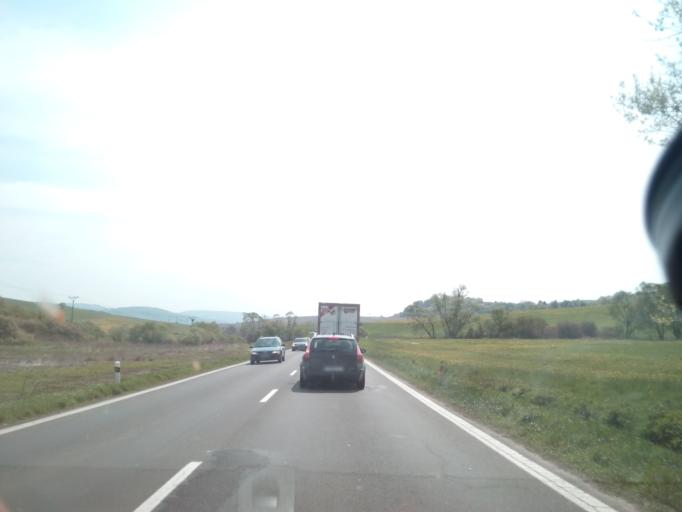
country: SK
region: Presovsky
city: Giraltovce
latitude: 49.0338
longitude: 21.4691
